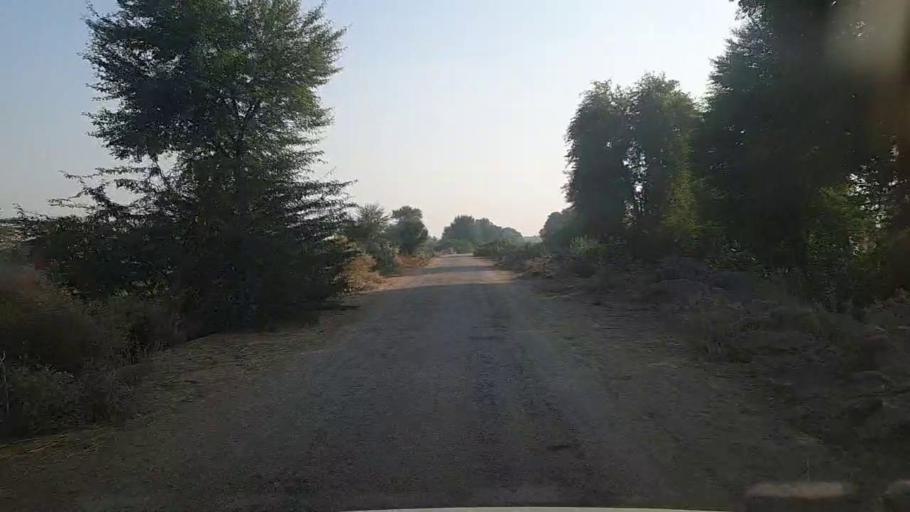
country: PK
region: Sindh
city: Karaundi
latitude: 26.7483
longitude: 68.4768
